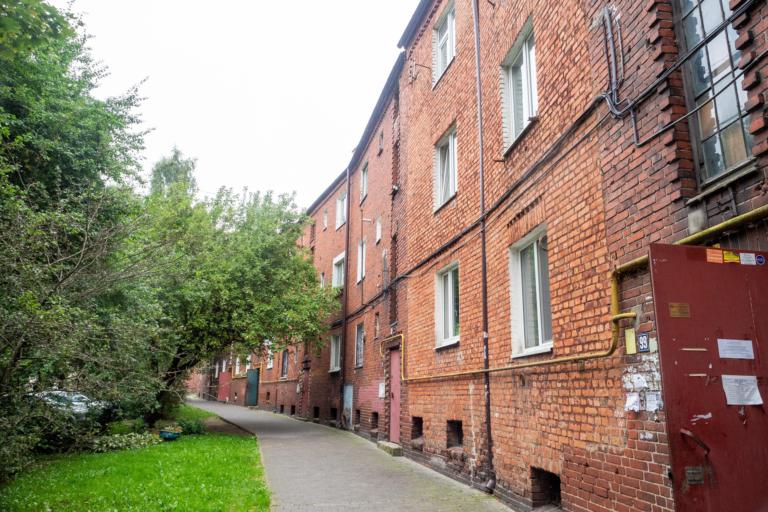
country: RU
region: Kaliningrad
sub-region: Gorod Kaliningrad
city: Kaliningrad
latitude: 54.7073
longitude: 20.5379
